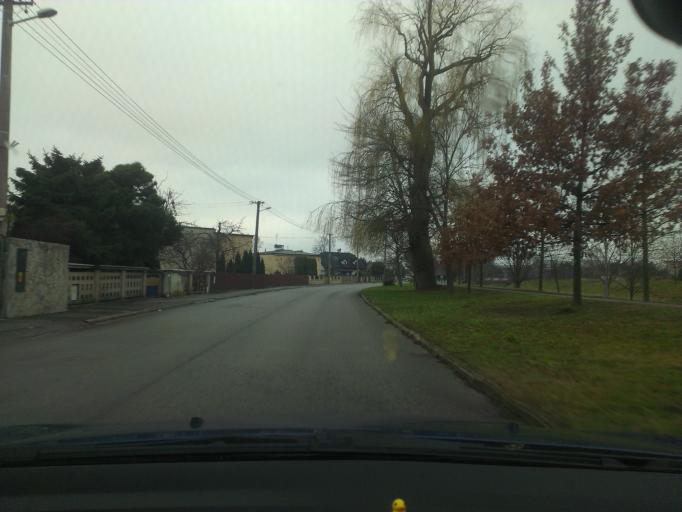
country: SK
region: Trnavsky
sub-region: Okres Trnava
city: Piestany
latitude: 48.5811
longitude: 17.8235
